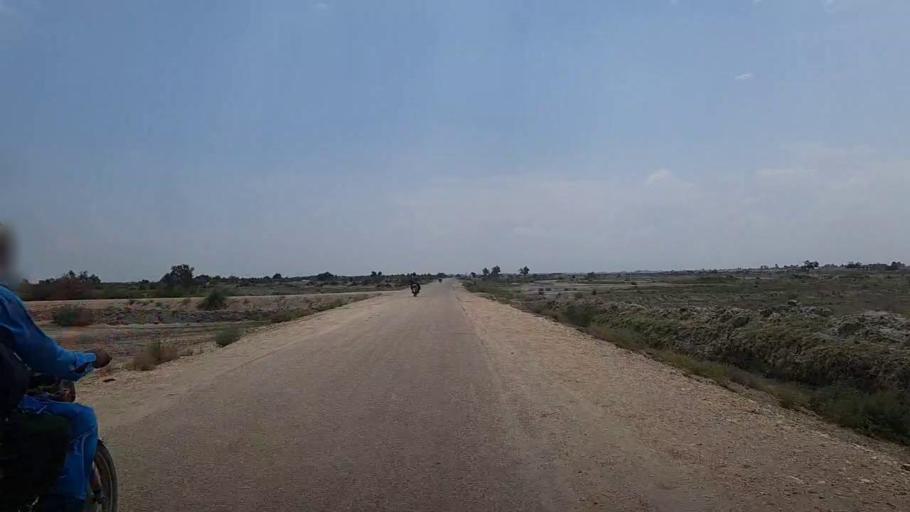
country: PK
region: Sindh
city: Kandhkot
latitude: 28.2911
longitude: 69.1435
